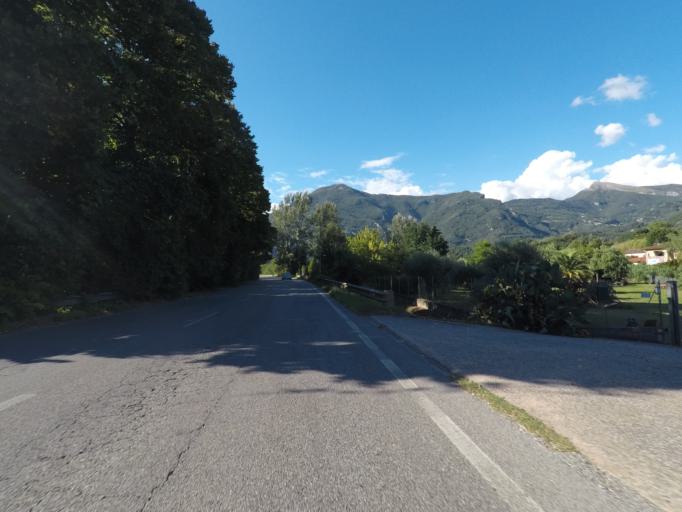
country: IT
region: Tuscany
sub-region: Provincia di Lucca
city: Corsanico-Bargecchia
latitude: 43.9310
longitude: 10.3114
